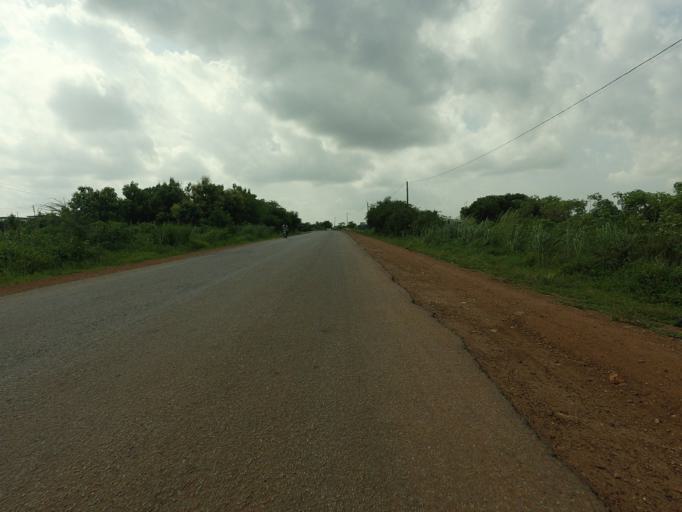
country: GH
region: Volta
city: Ho
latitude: 6.4250
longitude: 0.7345
